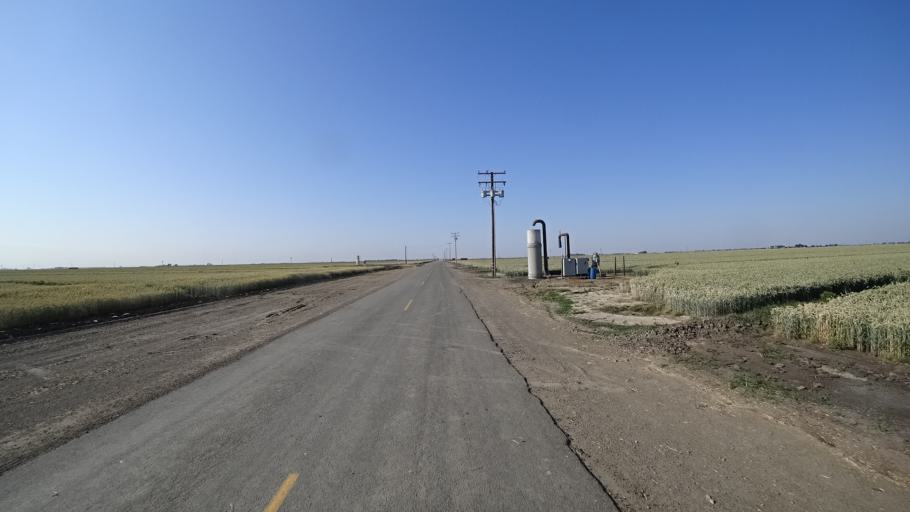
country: US
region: California
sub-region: Kings County
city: Home Garden
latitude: 36.2600
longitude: -119.5294
